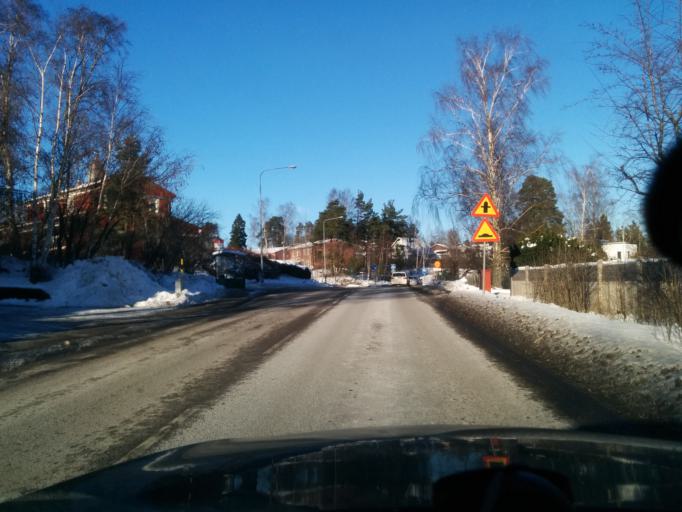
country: SE
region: Stockholm
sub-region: Taby Kommun
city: Taby
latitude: 59.4586
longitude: 18.0860
